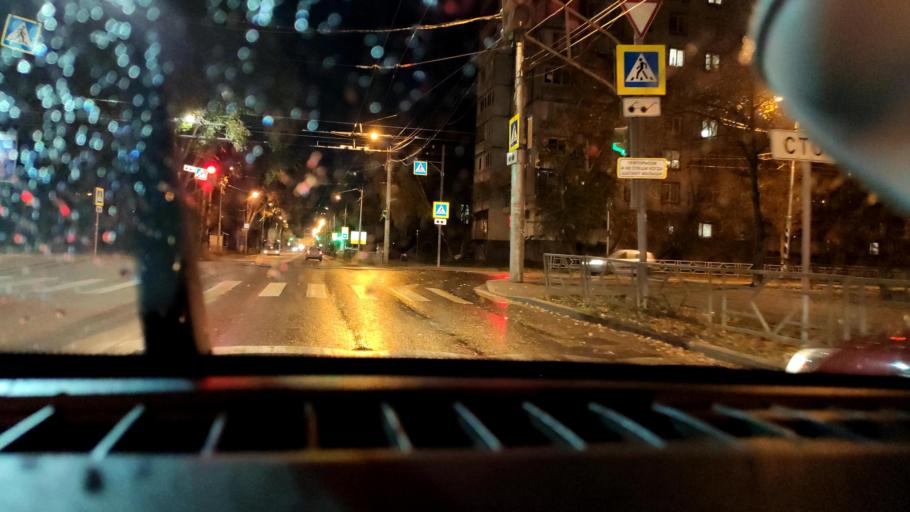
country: RU
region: Samara
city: Samara
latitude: 53.1992
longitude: 50.1378
